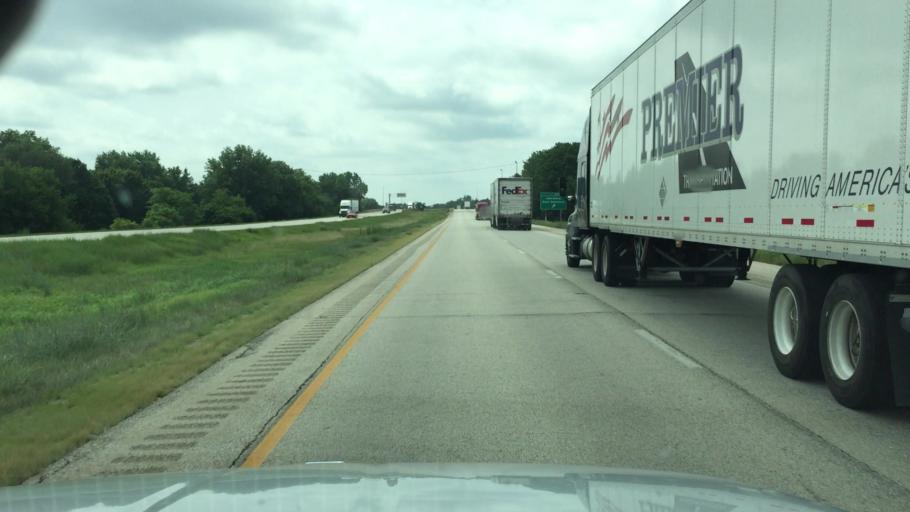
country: US
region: Illinois
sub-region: Knox County
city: Galesburg
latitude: 40.9525
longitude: -90.3330
